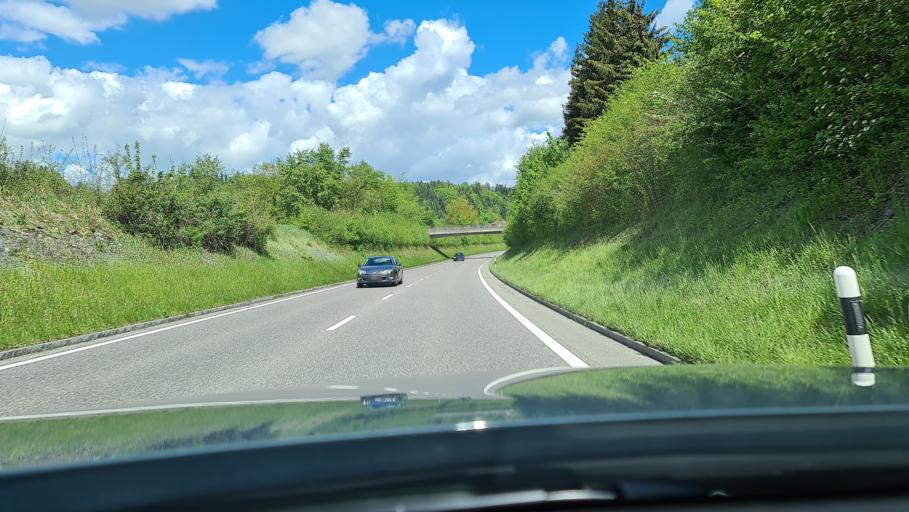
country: CH
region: Aargau
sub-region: Bezirk Kulm
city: Schoftland
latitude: 47.2987
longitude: 8.0445
